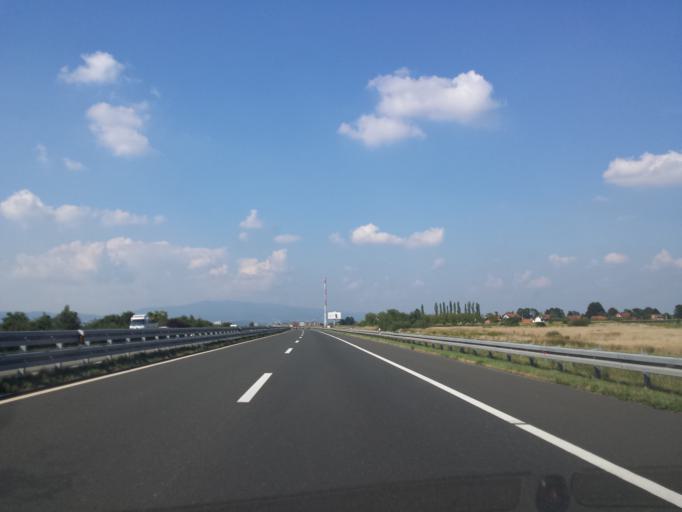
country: HR
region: Grad Zagreb
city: Brezovica
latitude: 45.7291
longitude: 15.8737
